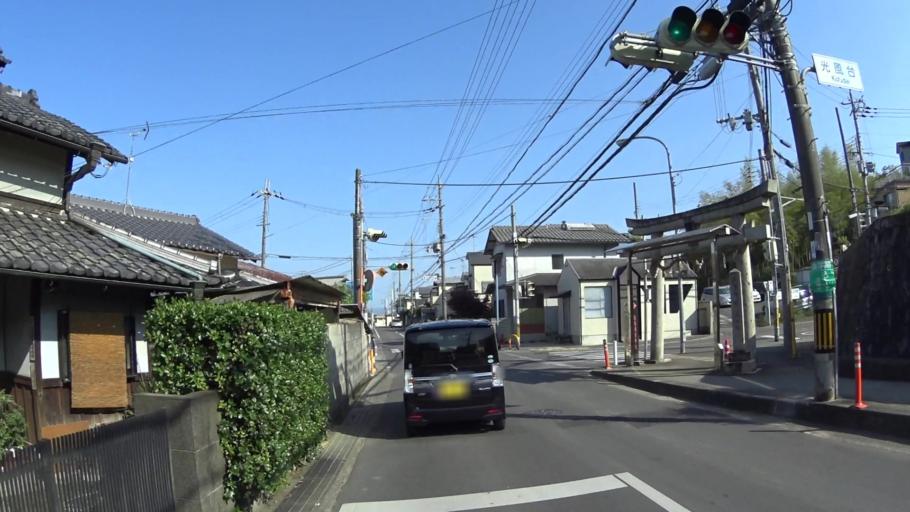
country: JP
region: Kyoto
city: Muko
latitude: 34.9309
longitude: 135.6805
